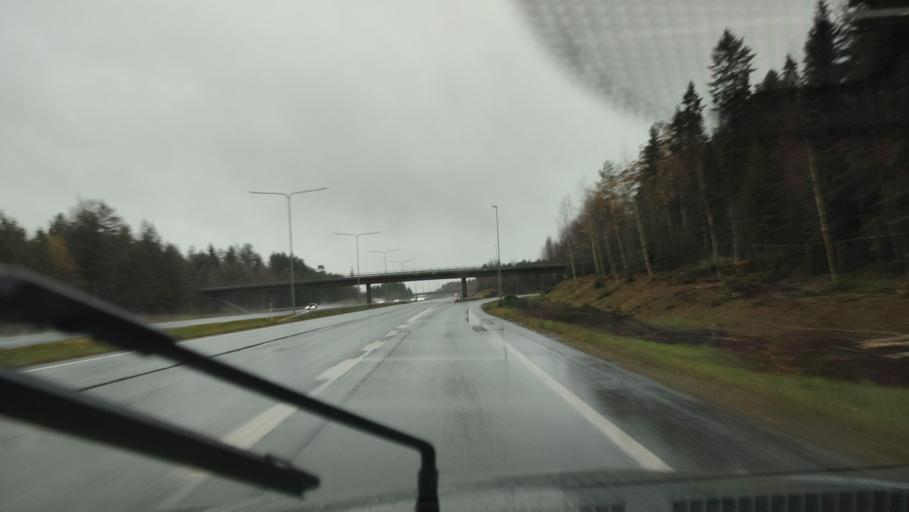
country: FI
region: Ostrobothnia
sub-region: Vaasa
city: Ristinummi
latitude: 63.0594
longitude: 21.7099
